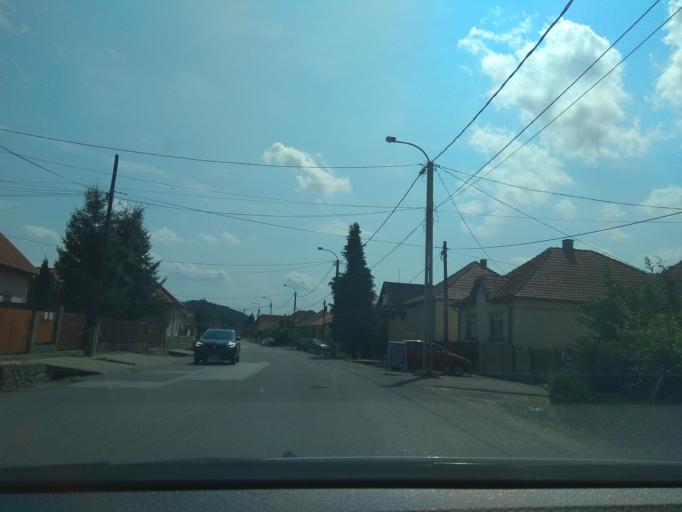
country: HU
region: Heves
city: Andornaktalya
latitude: 47.8570
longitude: 20.4067
